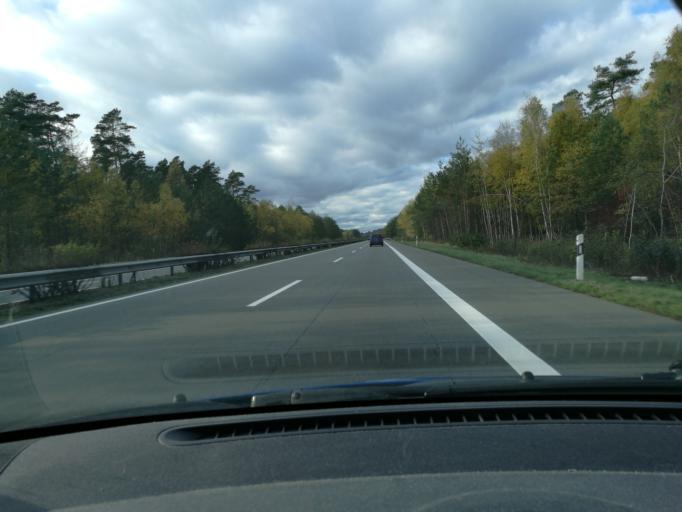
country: DE
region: Lower Saxony
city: Radbruch
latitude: 53.3183
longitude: 10.3107
